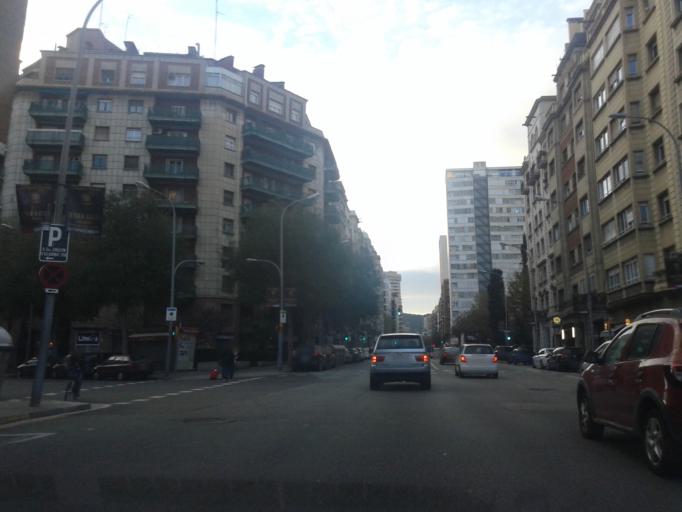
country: ES
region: Catalonia
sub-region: Provincia de Barcelona
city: Barcelona
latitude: 41.3901
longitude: 2.1465
